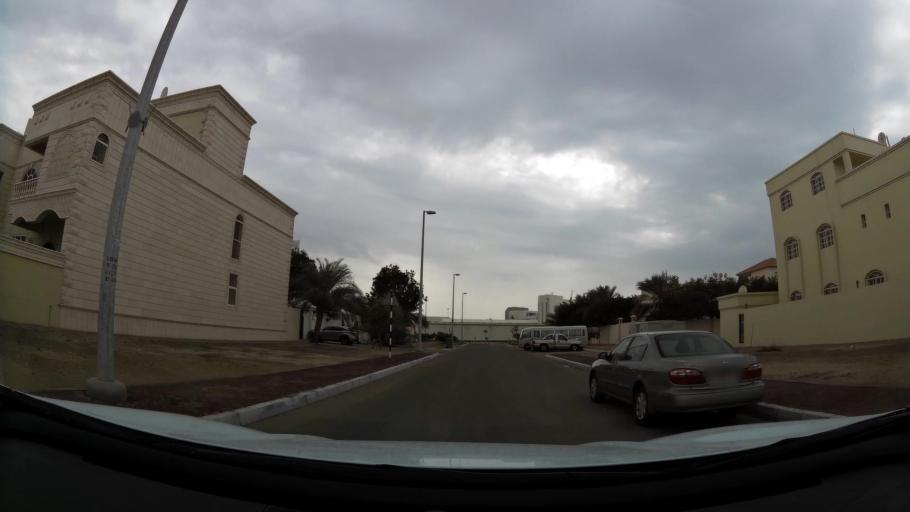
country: AE
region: Abu Dhabi
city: Abu Dhabi
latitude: 24.4246
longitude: 54.4253
